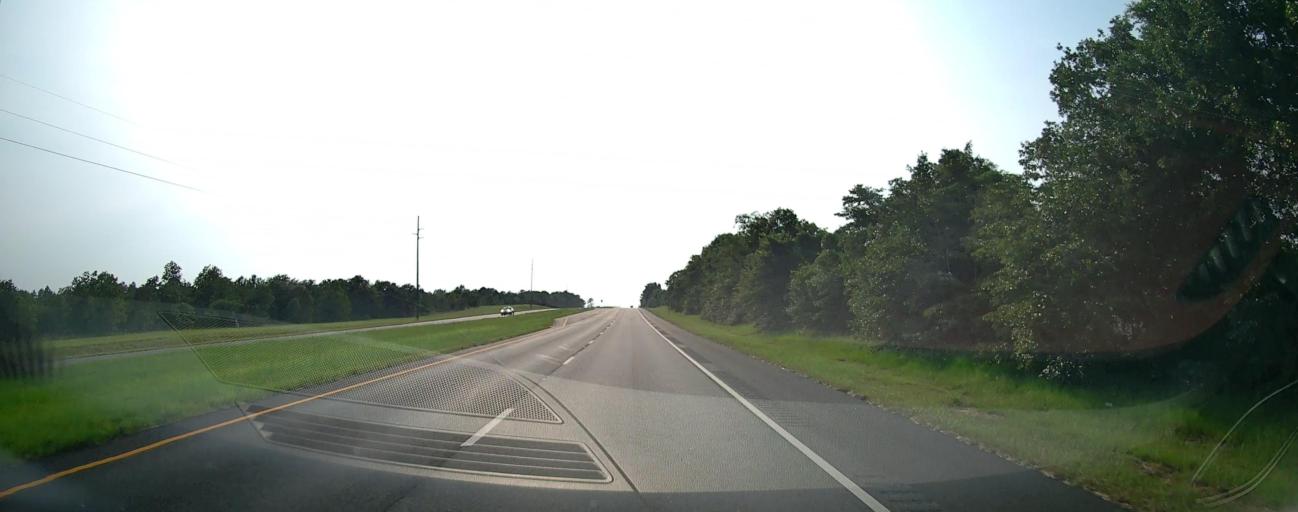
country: US
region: Georgia
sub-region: Taylor County
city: Butler
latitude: 32.5855
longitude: -84.3416
